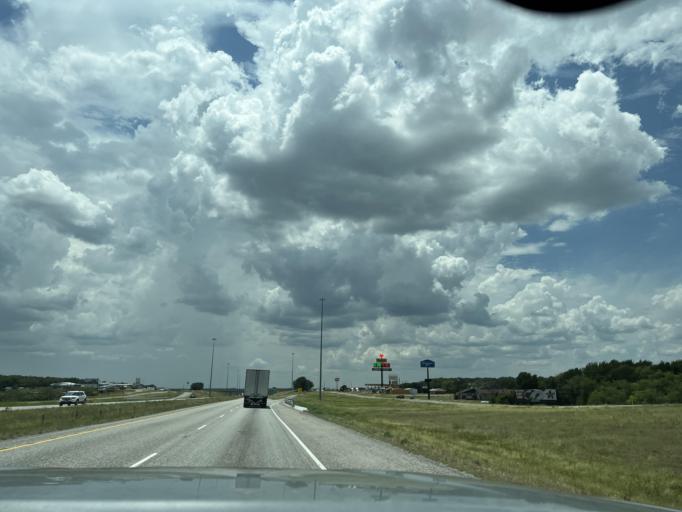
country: US
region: Texas
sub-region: Eastland County
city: Ranger
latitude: 32.4426
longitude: -98.6897
